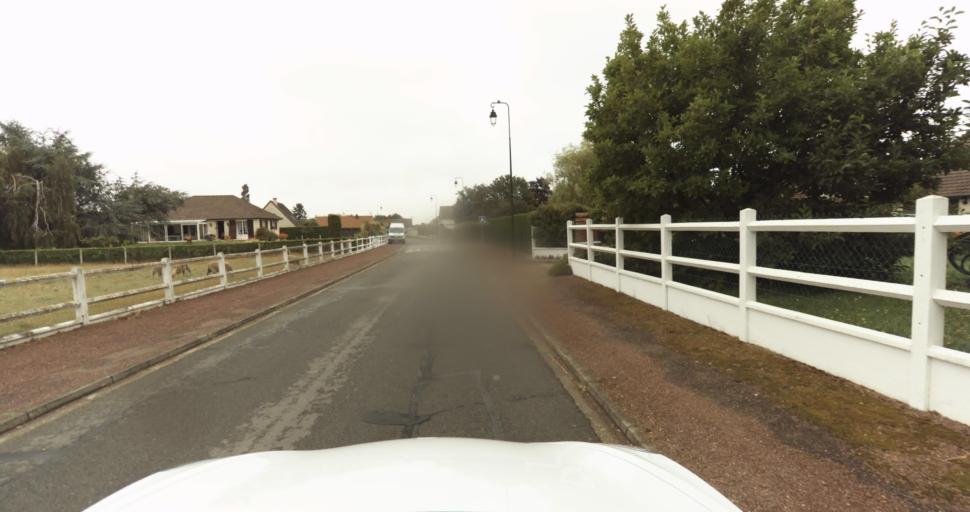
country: FR
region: Haute-Normandie
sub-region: Departement de l'Eure
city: Aviron
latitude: 49.0759
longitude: 1.0897
